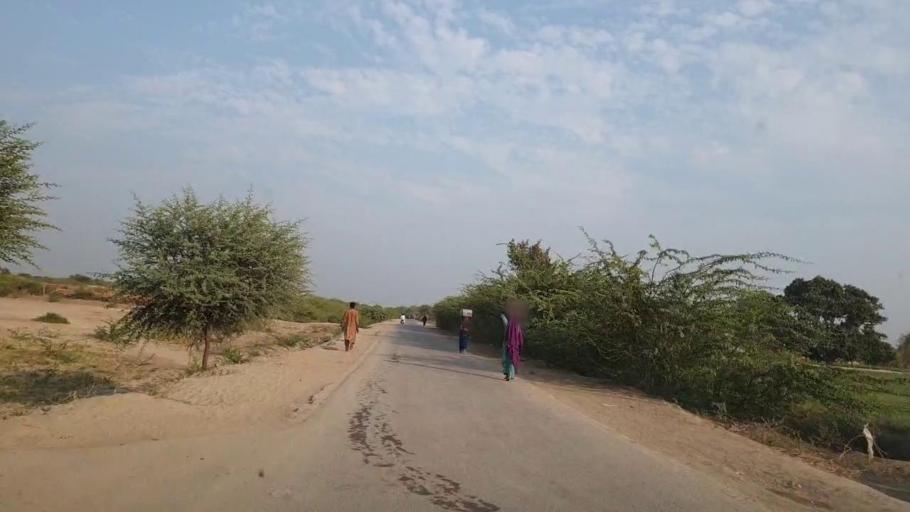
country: PK
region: Sindh
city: Pithoro
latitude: 25.5831
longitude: 69.3539
